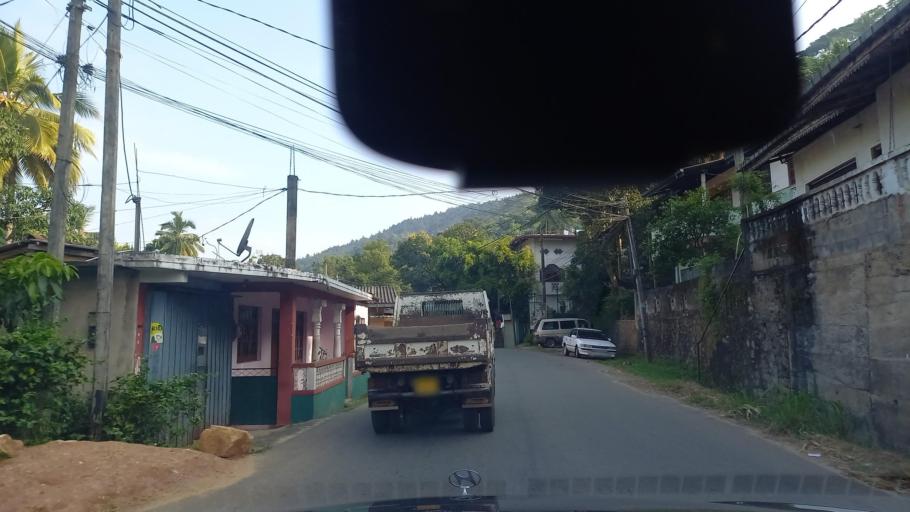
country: LK
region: Central
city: Kandy
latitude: 7.2333
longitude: 80.6024
